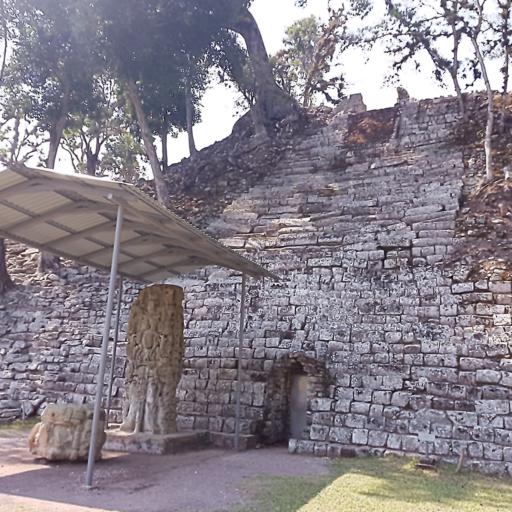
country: HN
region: Copan
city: Copan
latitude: 14.8385
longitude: -89.1419
